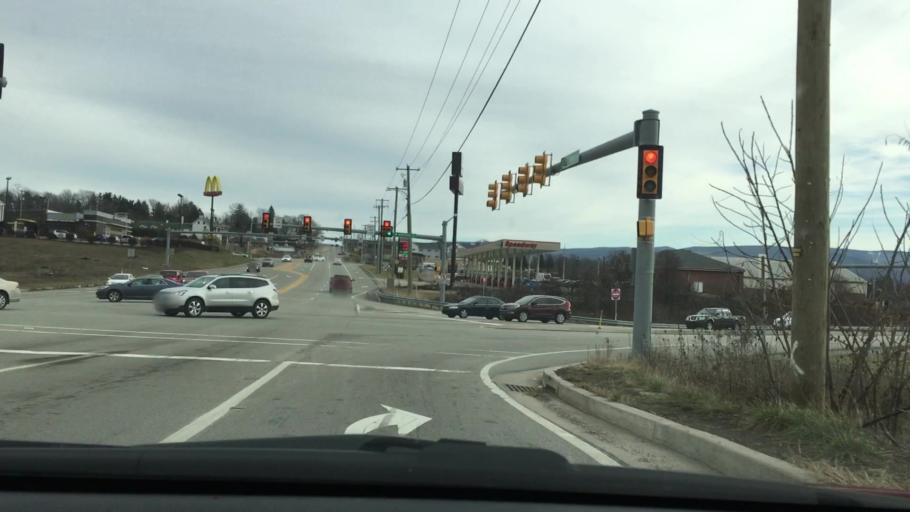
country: US
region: Pennsylvania
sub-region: Fayette County
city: South Uniontown
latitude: 39.9022
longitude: -79.7551
